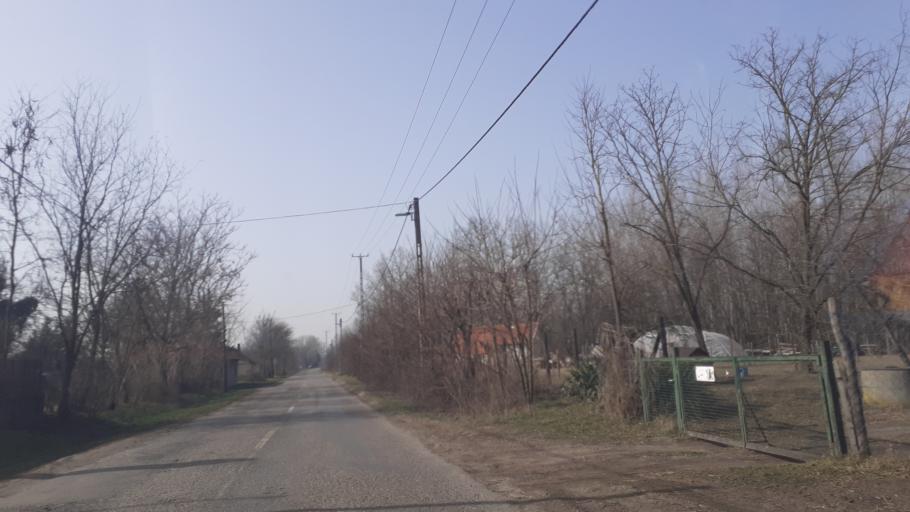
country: HU
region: Bacs-Kiskun
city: Kunszentmiklos
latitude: 47.0218
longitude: 19.2028
